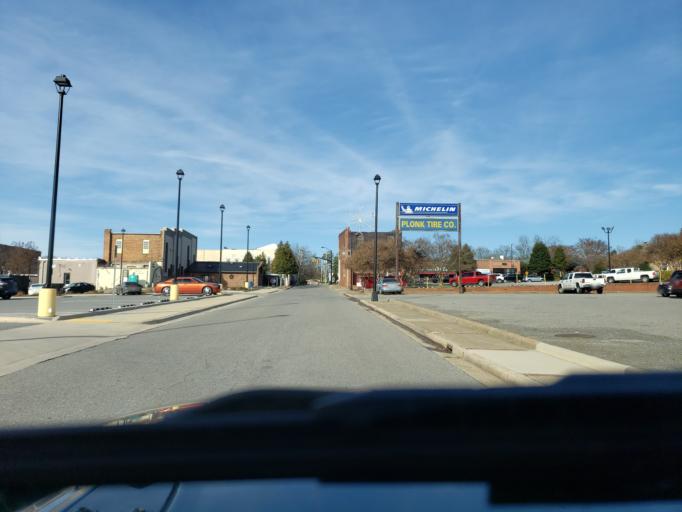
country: US
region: North Carolina
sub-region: Cleveland County
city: Kings Mountain
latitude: 35.2382
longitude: -81.3435
